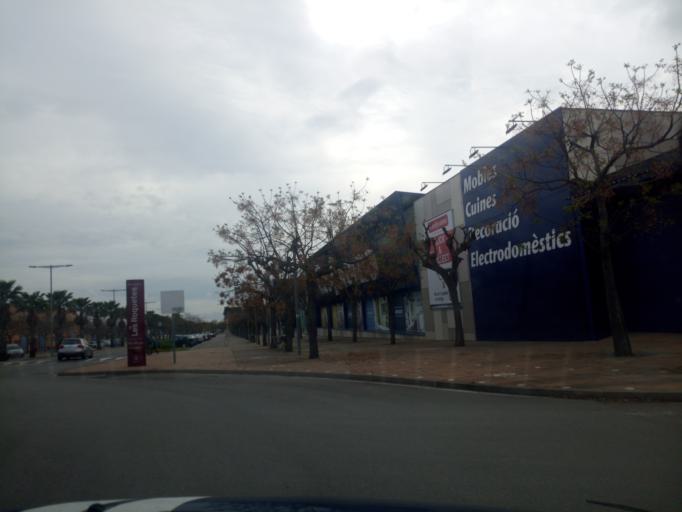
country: ES
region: Catalonia
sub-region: Provincia de Barcelona
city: Sant Pere de Ribes
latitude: 41.2290
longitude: 1.7667
